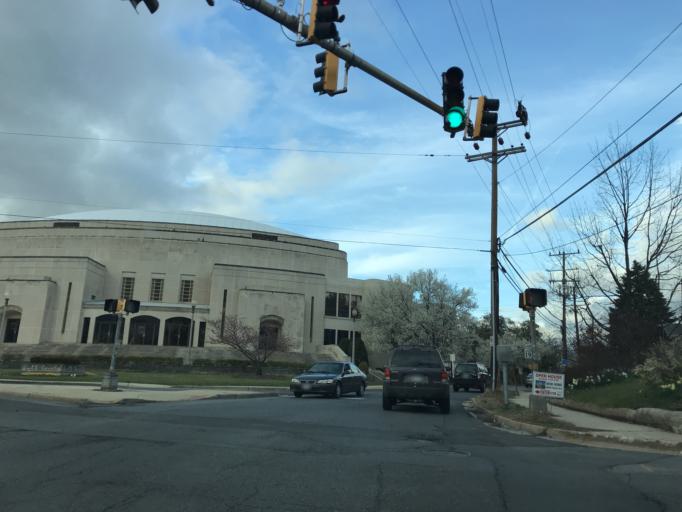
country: US
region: Maryland
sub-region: Montgomery County
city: Takoma Park
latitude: 38.9846
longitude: -76.9987
